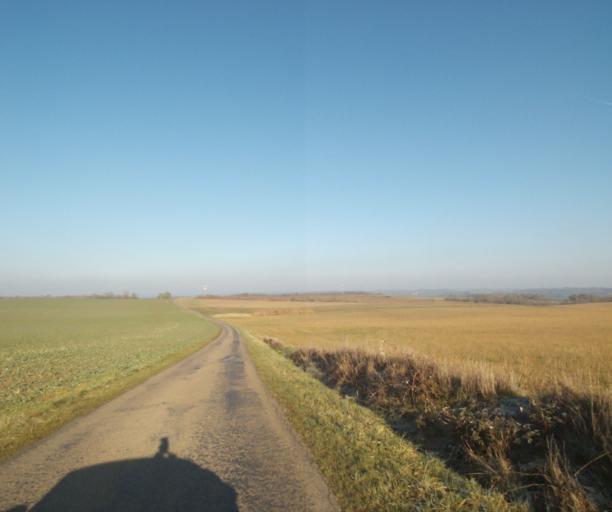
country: FR
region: Champagne-Ardenne
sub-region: Departement de la Haute-Marne
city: Chevillon
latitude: 48.5081
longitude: 5.0847
